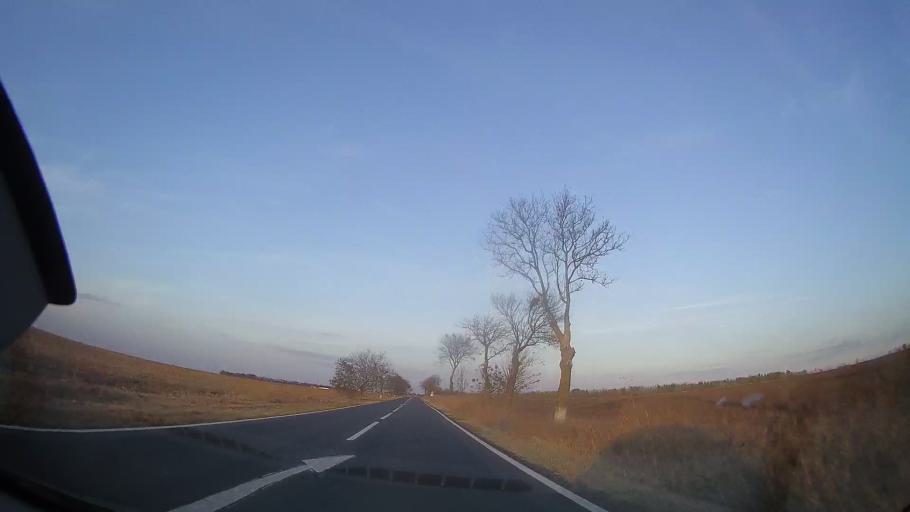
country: RO
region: Constanta
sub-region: Comuna Topraisar
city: Topraisar
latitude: 43.9972
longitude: 28.4310
